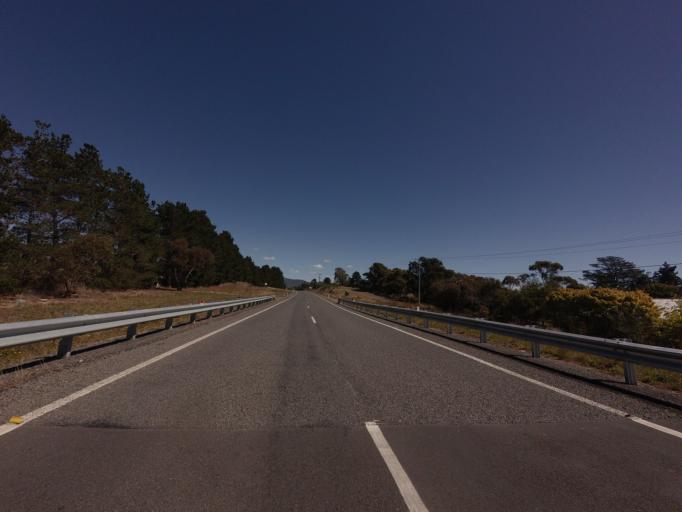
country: AU
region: Tasmania
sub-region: Northern Midlands
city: Evandale
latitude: -41.7843
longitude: 147.7184
